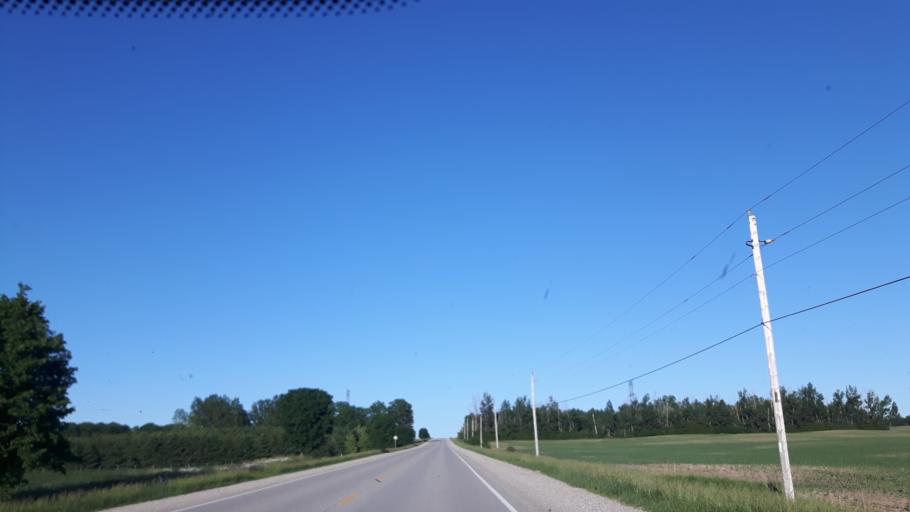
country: CA
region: Ontario
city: Goderich
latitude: 43.6426
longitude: -81.6418
